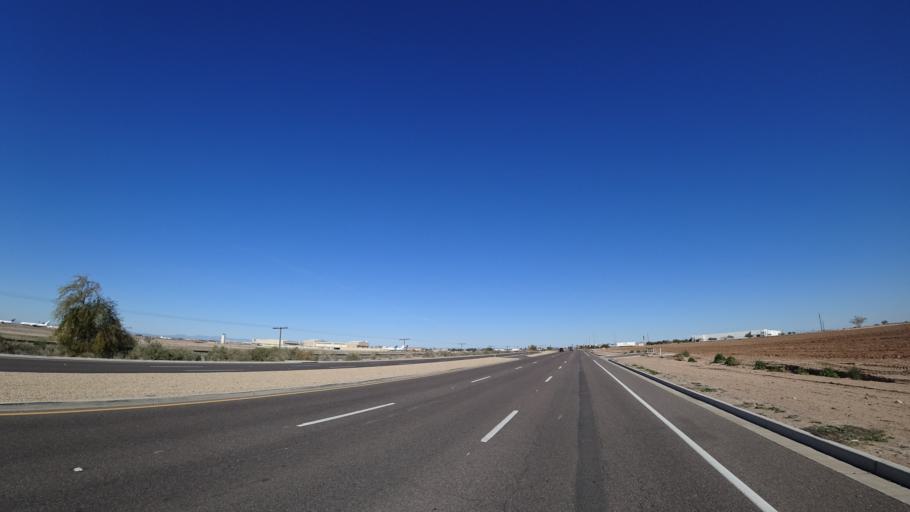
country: US
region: Arizona
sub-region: Maricopa County
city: Goodyear
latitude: 33.4179
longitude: -112.3696
